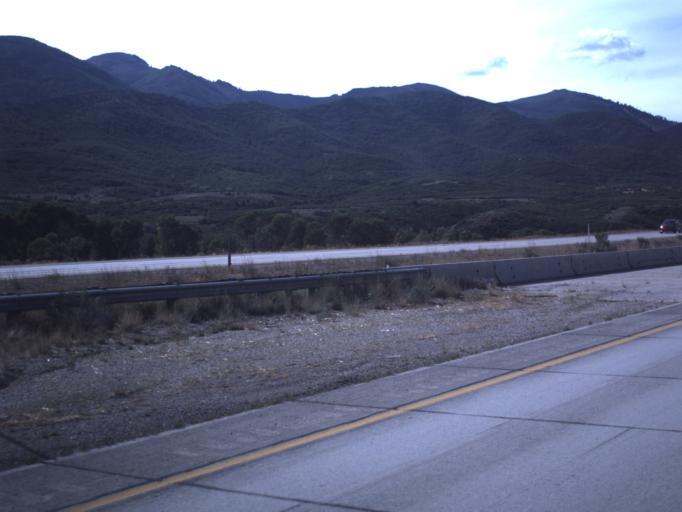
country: US
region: Utah
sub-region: Wasatch County
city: Heber
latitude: 40.5691
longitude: -111.4302
